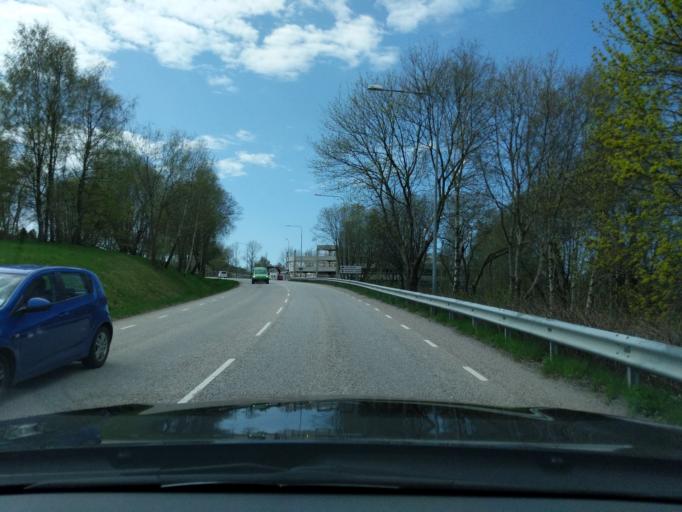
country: SE
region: Vaestra Goetaland
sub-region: Goteborg
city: Majorna
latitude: 57.6384
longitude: 11.9472
